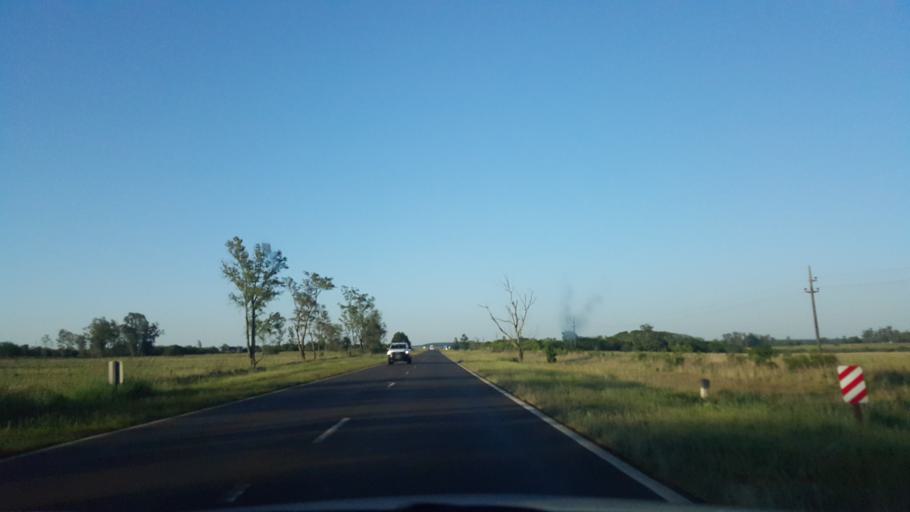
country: AR
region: Corrientes
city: Santo Tome
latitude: -28.4842
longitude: -56.1149
